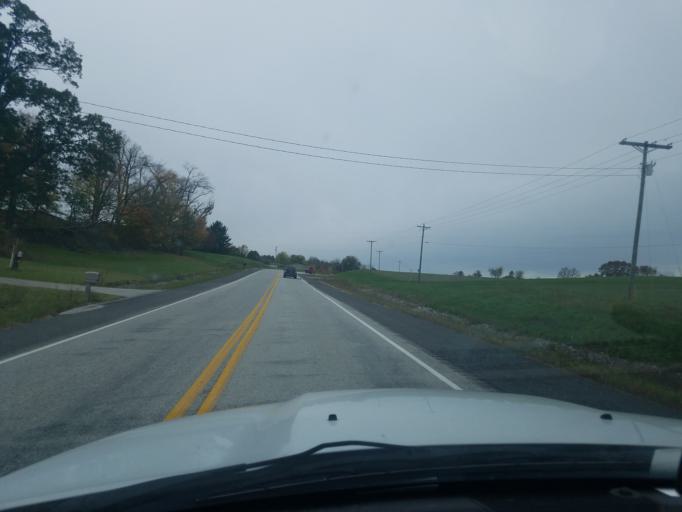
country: US
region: Indiana
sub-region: Washington County
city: Salem
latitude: 38.5478
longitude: -86.0939
